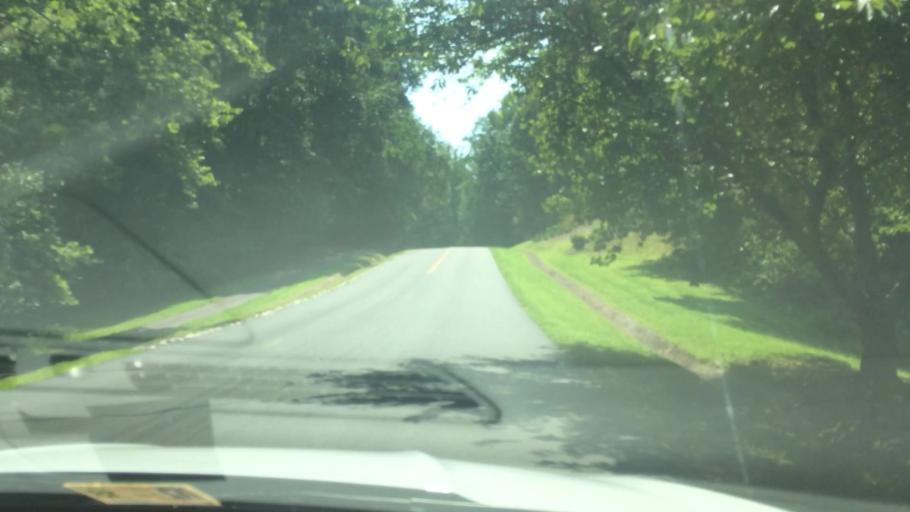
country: US
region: Virginia
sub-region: James City County
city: Williamsburg
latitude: 37.2980
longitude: -76.7696
